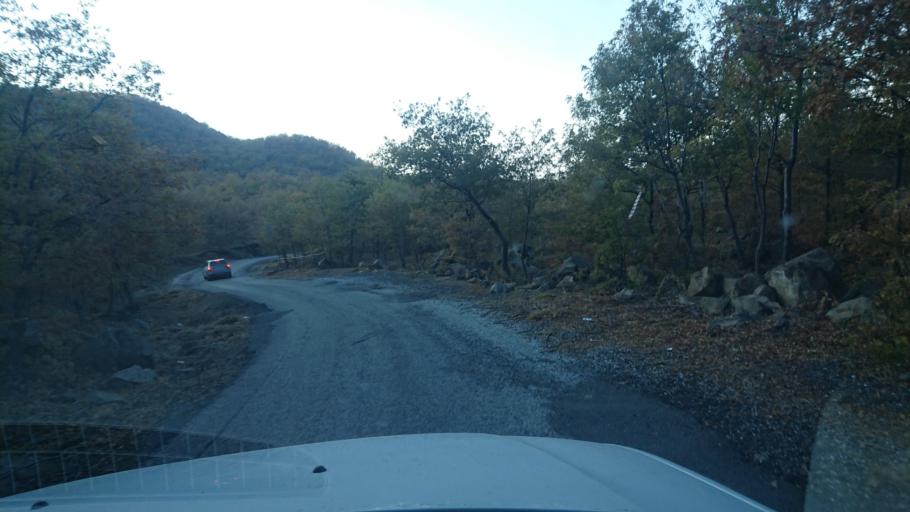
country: TR
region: Aksaray
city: Taspinar
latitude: 38.1665
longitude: 34.1957
